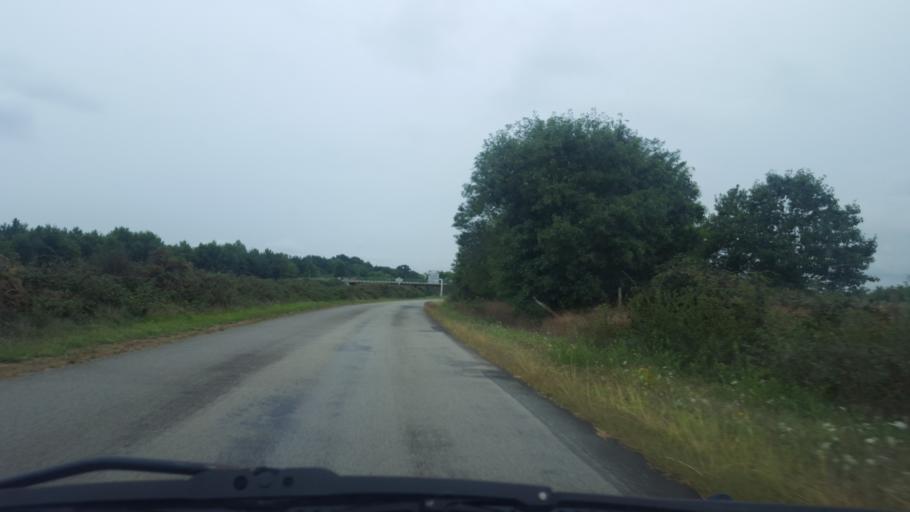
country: FR
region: Pays de la Loire
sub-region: Departement de la Loire-Atlantique
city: Saint-Philbert-de-Grand-Lieu
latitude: 47.0351
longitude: -1.6558
